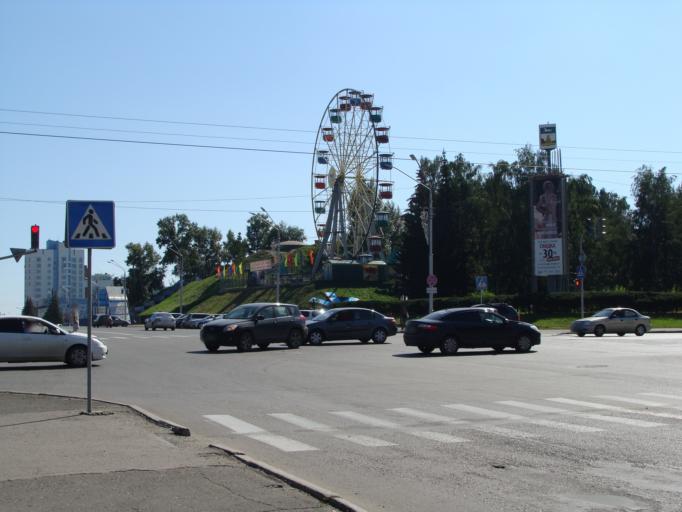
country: RU
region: Altai Krai
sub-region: Gorod Barnaulskiy
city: Barnaul
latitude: 53.3472
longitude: 83.7718
